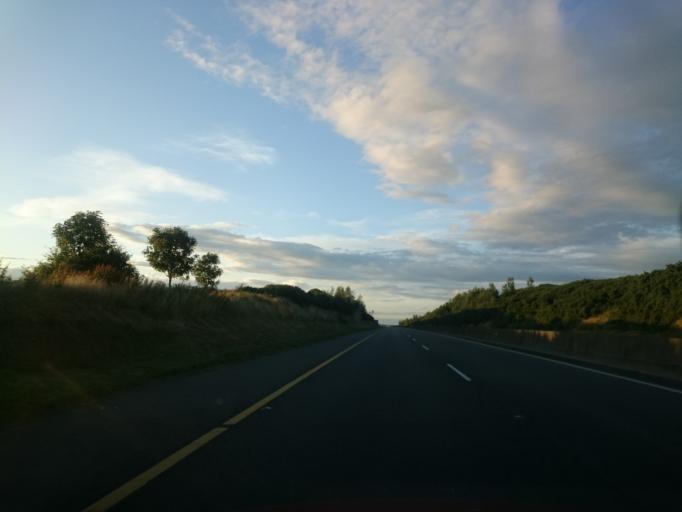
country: IE
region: Leinster
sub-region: Loch Garman
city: Gorey
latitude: 52.6940
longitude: -6.2636
